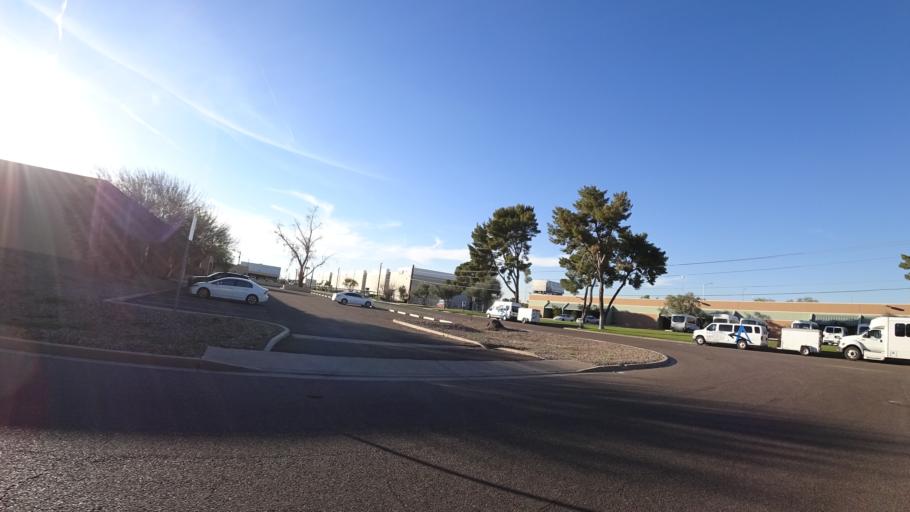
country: US
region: Arizona
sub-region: Maricopa County
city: Phoenix
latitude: 33.4255
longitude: -112.0392
